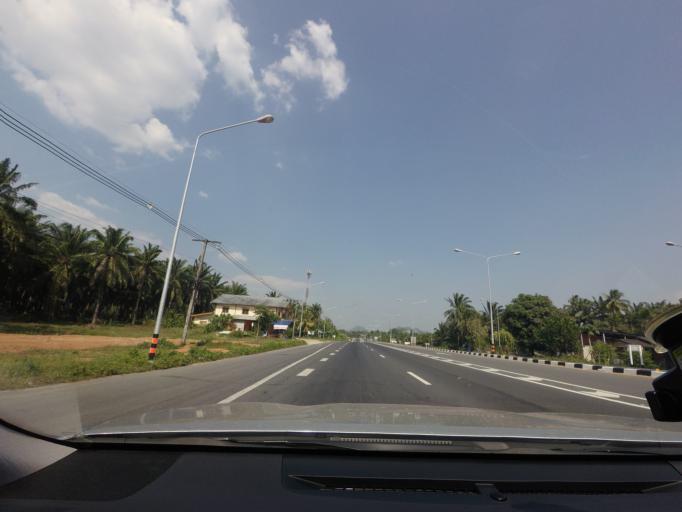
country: TH
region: Phangnga
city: Thap Put
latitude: 8.5402
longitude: 98.7193
